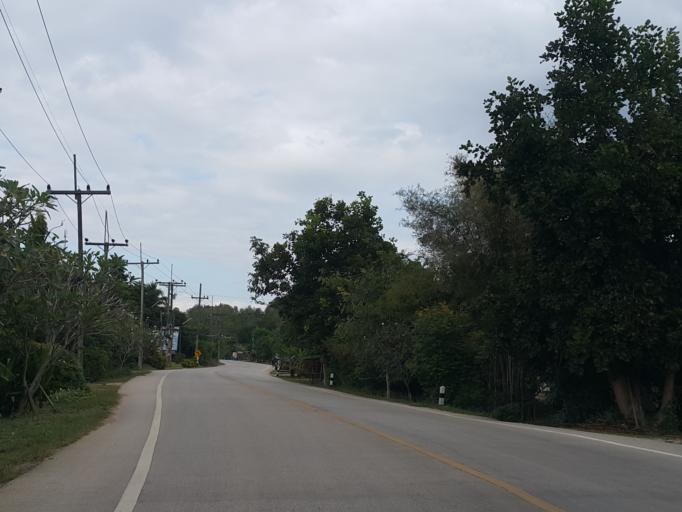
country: TH
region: Lampang
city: Chae Hom
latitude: 18.5834
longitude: 99.4718
